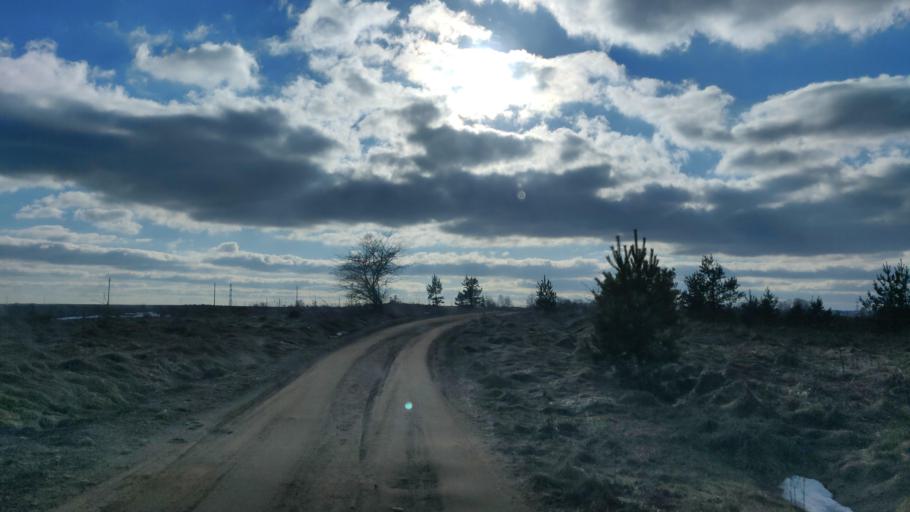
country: LT
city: Lentvaris
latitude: 54.6104
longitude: 24.9986
